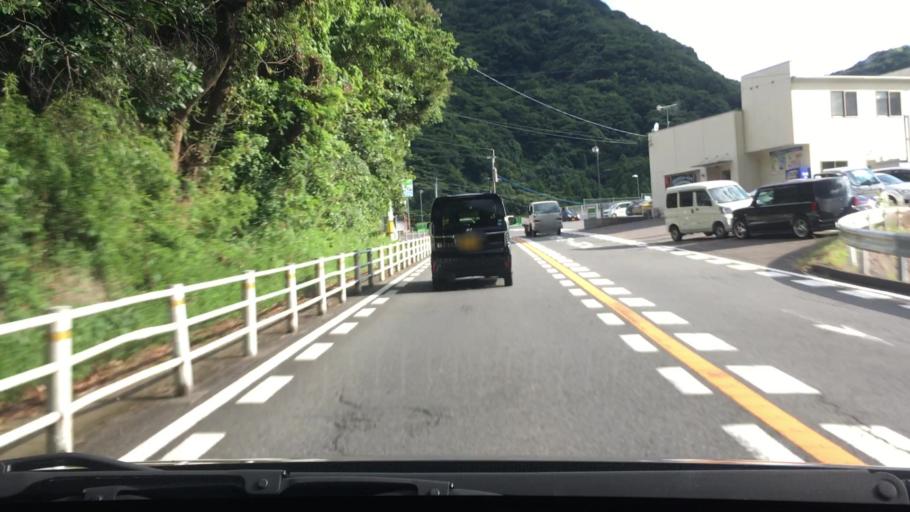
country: JP
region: Nagasaki
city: Togitsu
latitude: 32.8107
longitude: 129.8105
